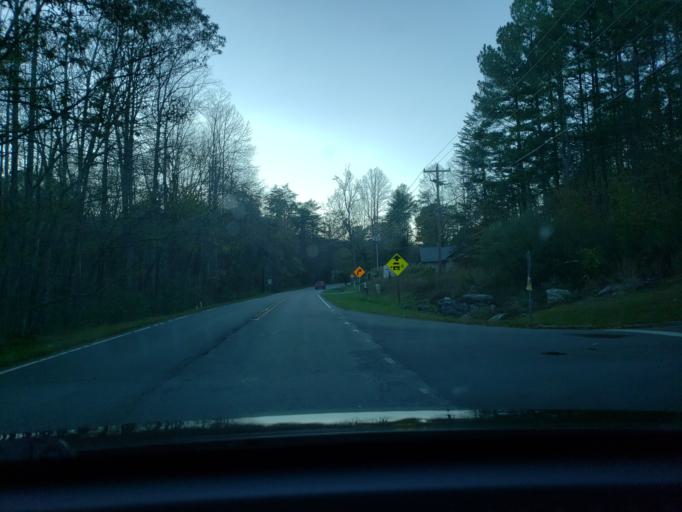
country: US
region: North Carolina
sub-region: Stokes County
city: Danbury
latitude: 36.4123
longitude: -80.2179
